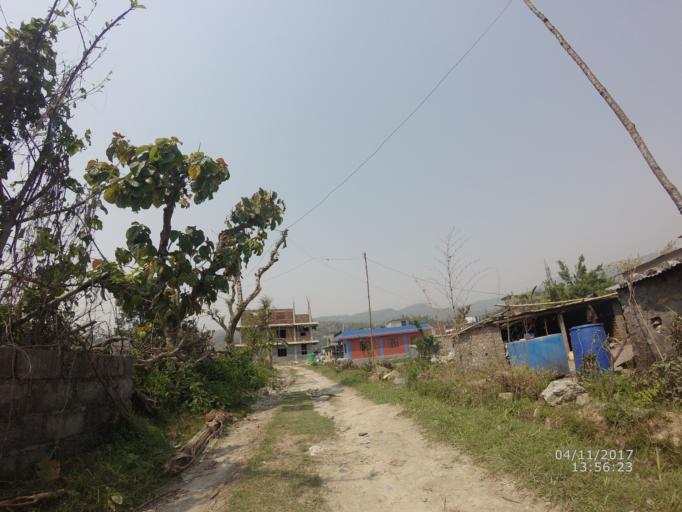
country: NP
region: Western Region
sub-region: Gandaki Zone
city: Pokhara
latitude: 28.1855
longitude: 84.0427
